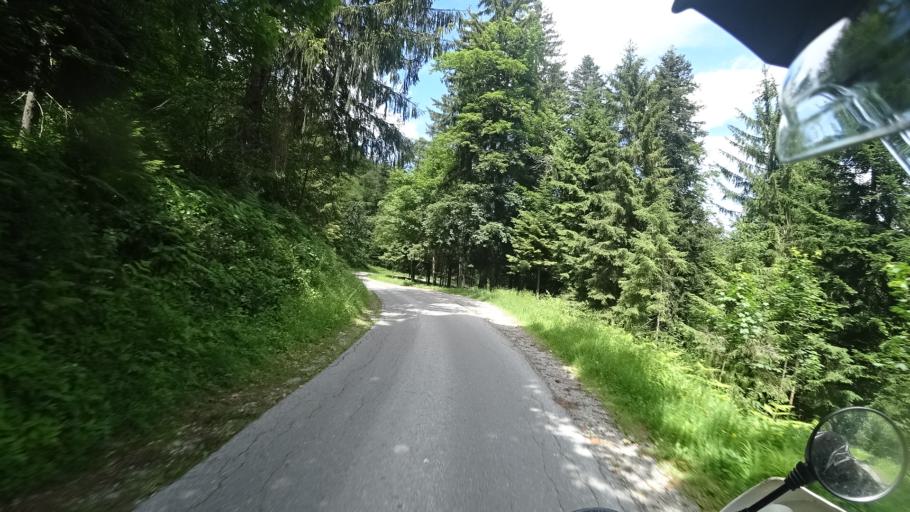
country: SI
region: Osilnica
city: Osilnica
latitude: 45.4977
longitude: 14.6263
